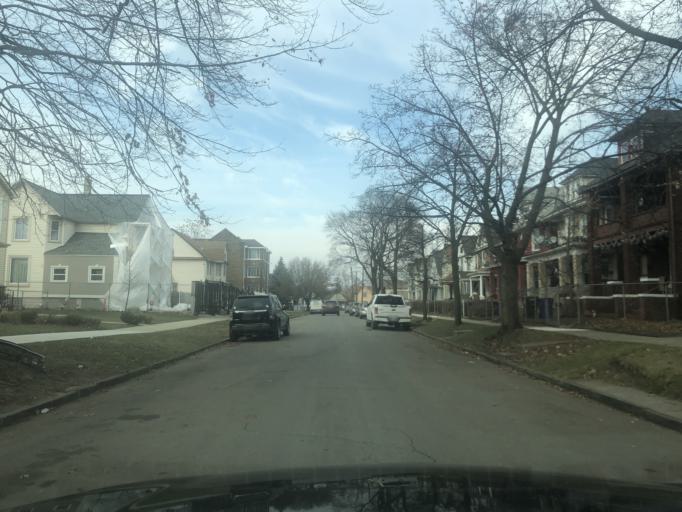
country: US
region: Michigan
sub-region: Wayne County
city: River Rouge
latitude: 42.3199
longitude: -83.1019
